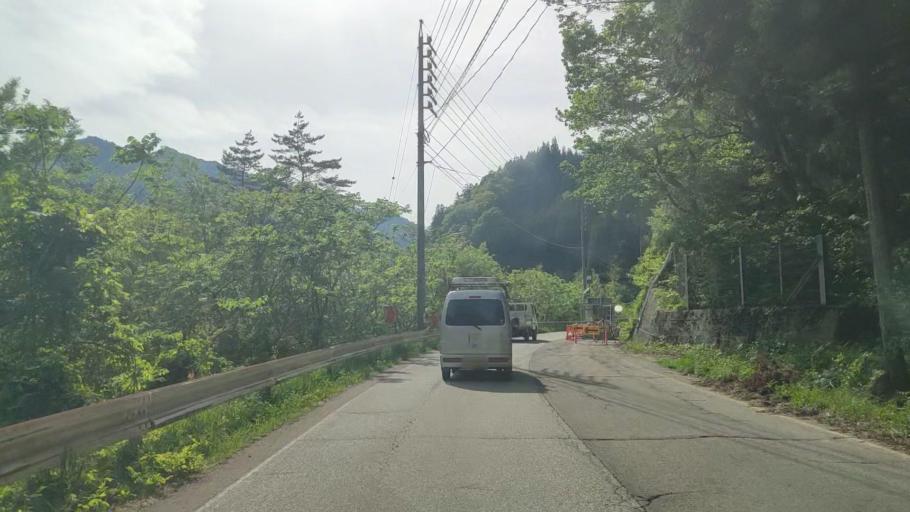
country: JP
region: Gifu
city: Takayama
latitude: 36.2688
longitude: 137.4122
